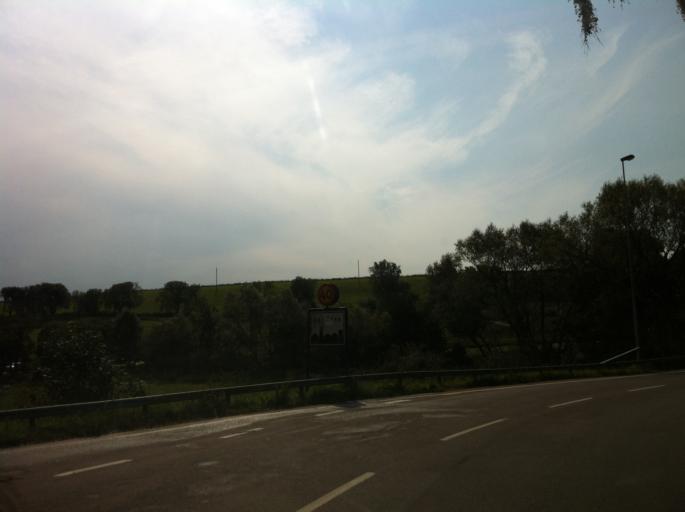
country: SE
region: Skane
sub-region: Helsingborg
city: Barslov
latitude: 55.9757
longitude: 12.8605
